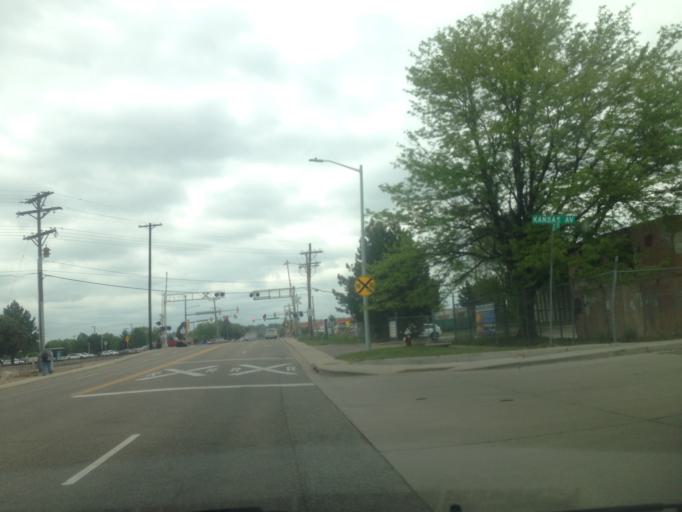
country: US
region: Colorado
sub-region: Boulder County
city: Longmont
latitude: 40.1472
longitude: -105.1214
